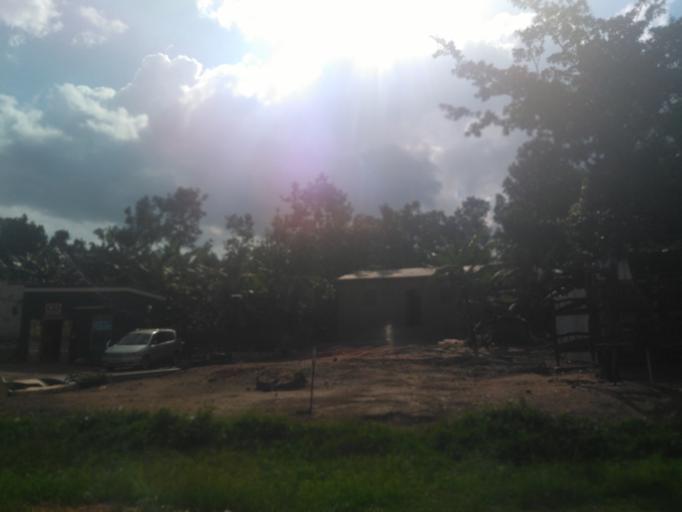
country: UG
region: Central Region
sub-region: Wakiso District
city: Kajansi
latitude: 0.2753
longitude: 32.4596
